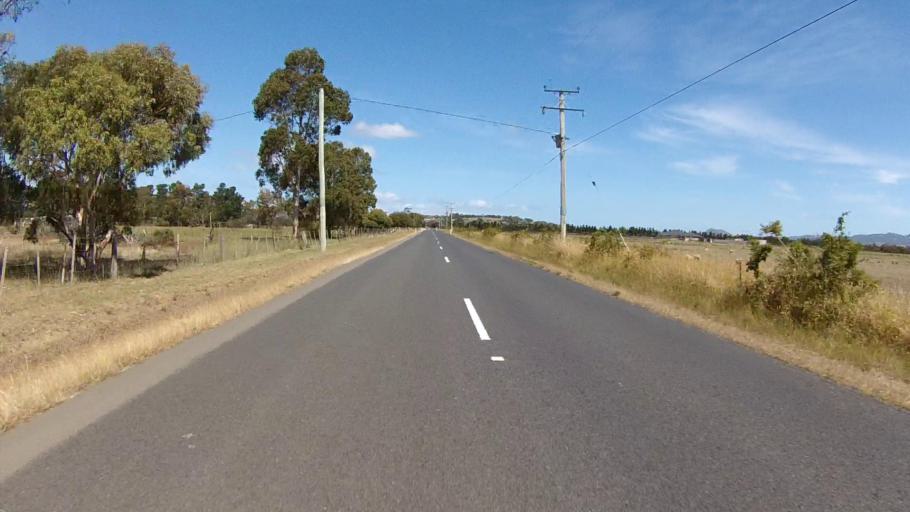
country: AU
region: Tasmania
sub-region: Sorell
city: Sorell
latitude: -42.7735
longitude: 147.5188
